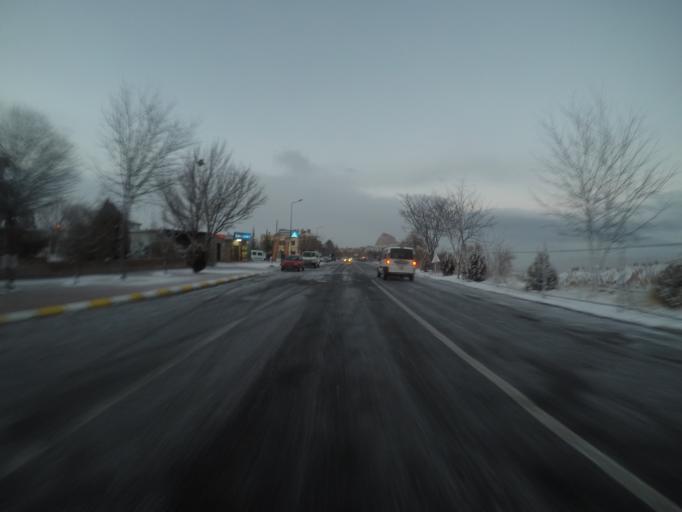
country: TR
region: Nevsehir
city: Goereme
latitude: 38.6217
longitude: 34.8043
